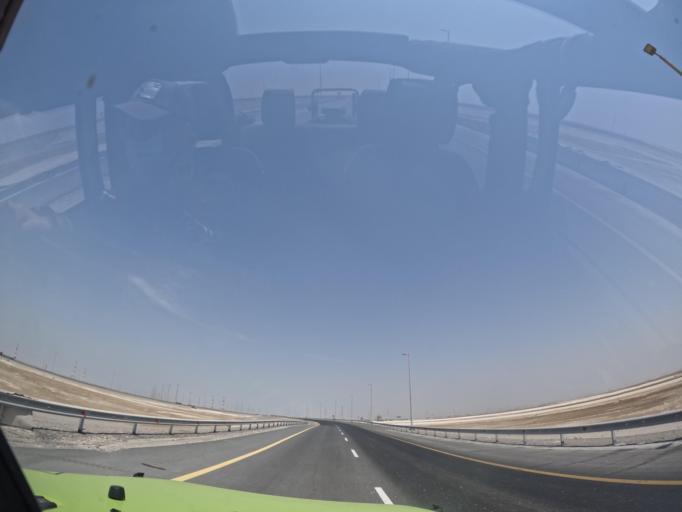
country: AE
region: Abu Dhabi
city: Abu Dhabi
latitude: 24.1463
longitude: 54.2404
